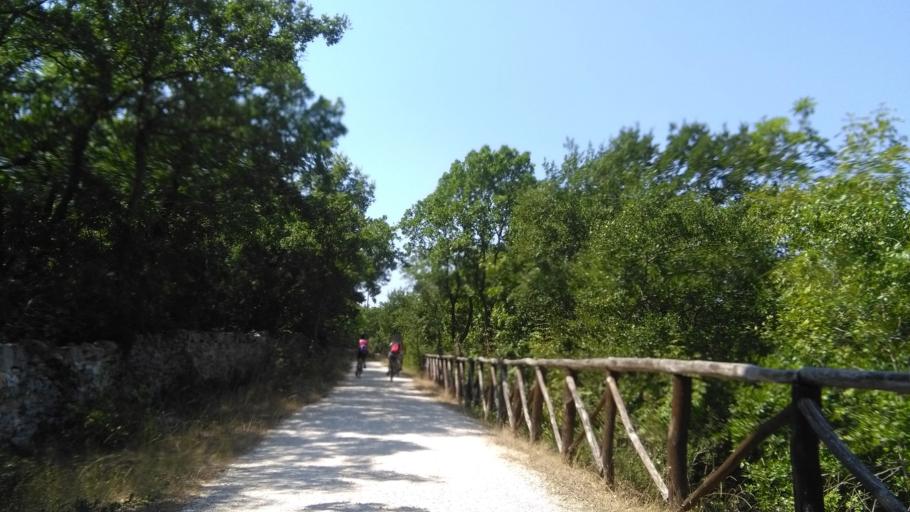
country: IT
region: Apulia
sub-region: Provincia di Brindisi
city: Cisternino
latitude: 40.6799
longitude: 17.4325
